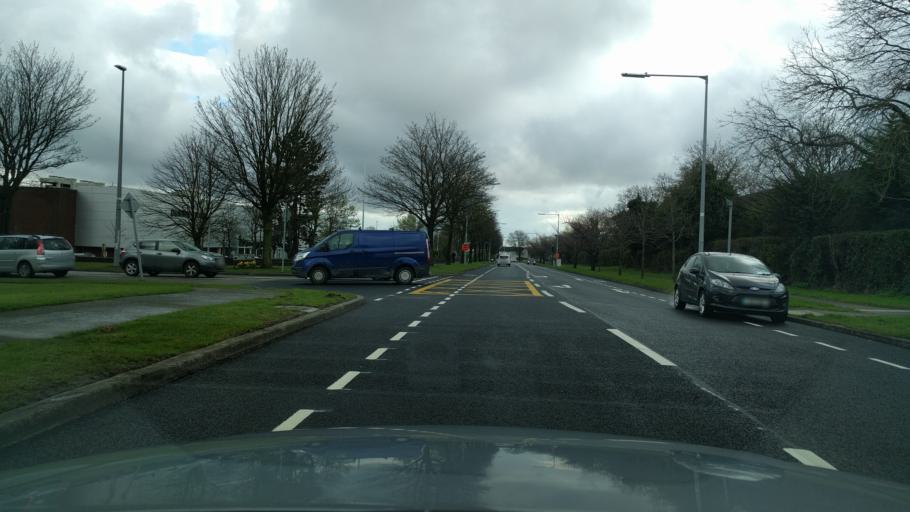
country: IE
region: Leinster
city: Tallaght
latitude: 53.2980
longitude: -6.3613
